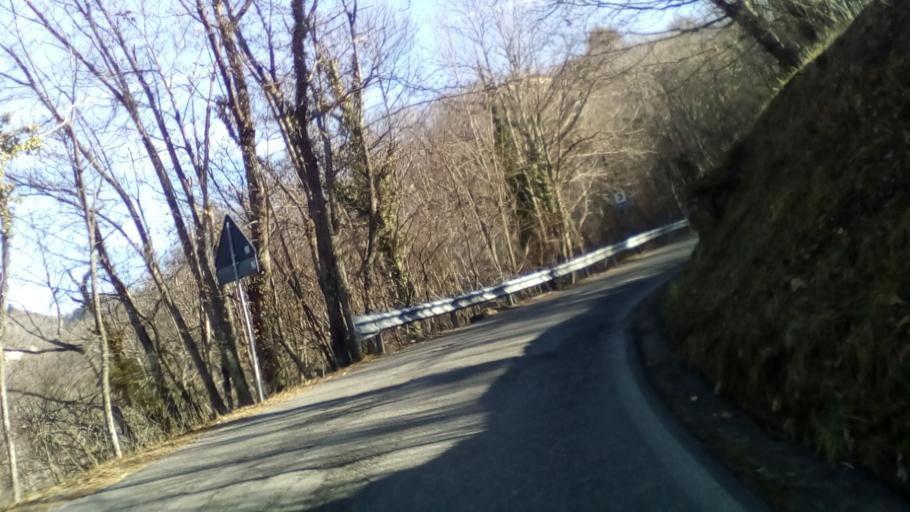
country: IT
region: Tuscany
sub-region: Provincia di Lucca
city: Castiglione di Garfagnana
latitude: 44.1429
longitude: 10.4316
